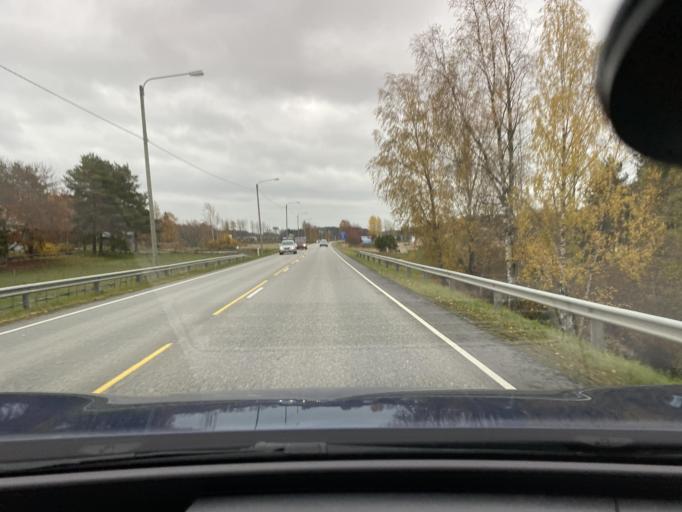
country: FI
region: Varsinais-Suomi
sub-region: Vakka-Suomi
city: Pyhaeranta
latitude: 60.9835
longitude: 21.5887
